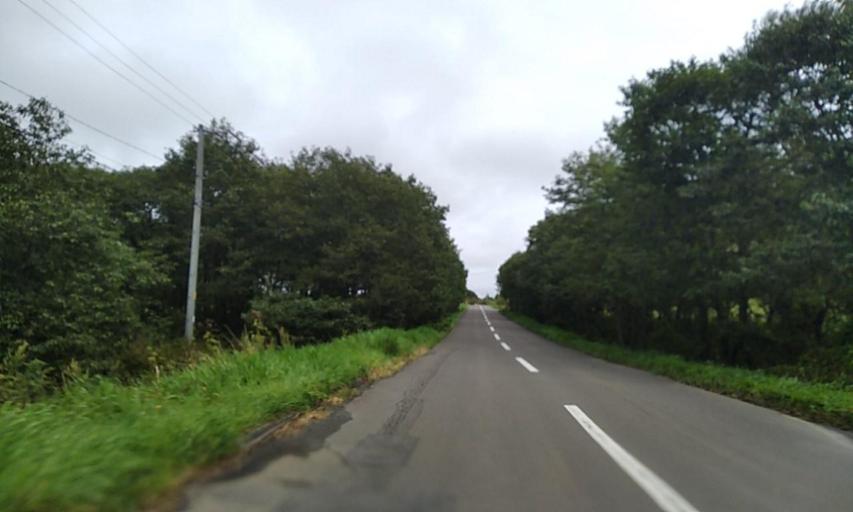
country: JP
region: Hokkaido
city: Nemuro
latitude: 43.2720
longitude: 145.2763
